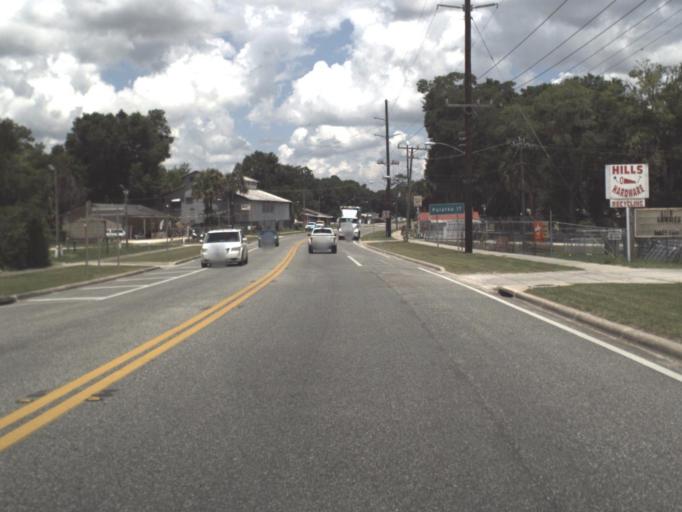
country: US
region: Florida
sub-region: Putnam County
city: Crescent City
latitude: 29.4967
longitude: -81.5946
